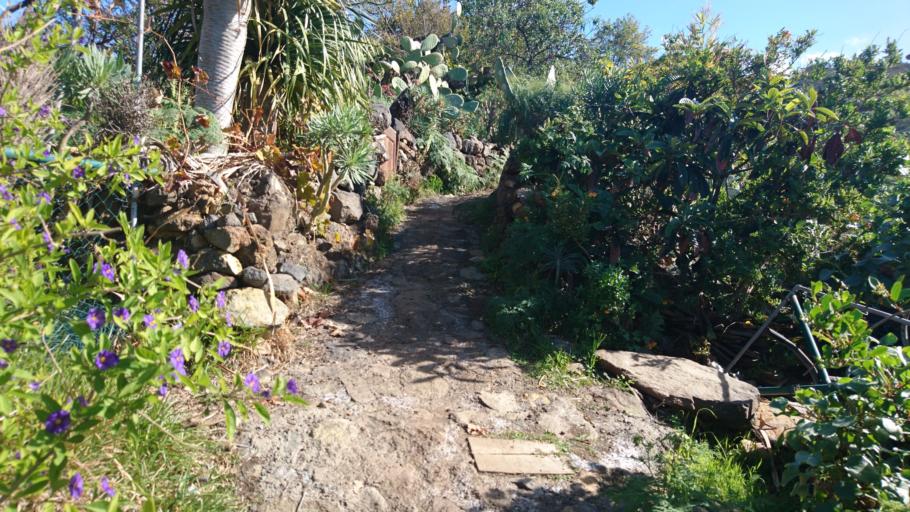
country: ES
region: Canary Islands
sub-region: Provincia de Santa Cruz de Tenerife
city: Puntagorda
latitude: 28.7928
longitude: -17.9772
